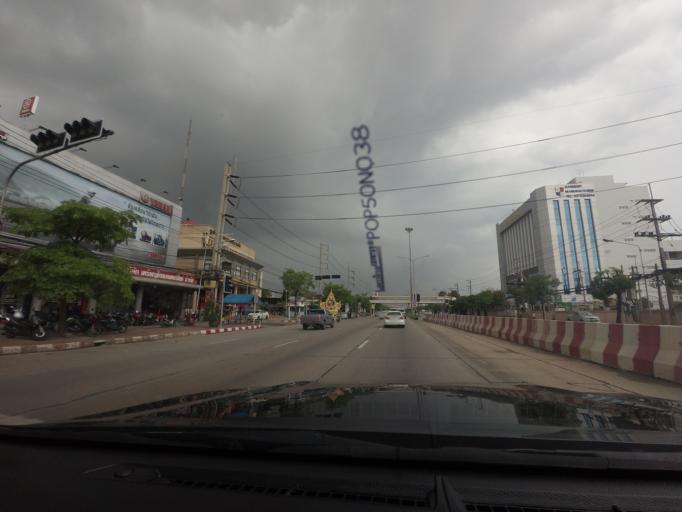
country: TH
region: Bangkok
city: Nong Khaem
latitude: 13.7048
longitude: 100.3147
